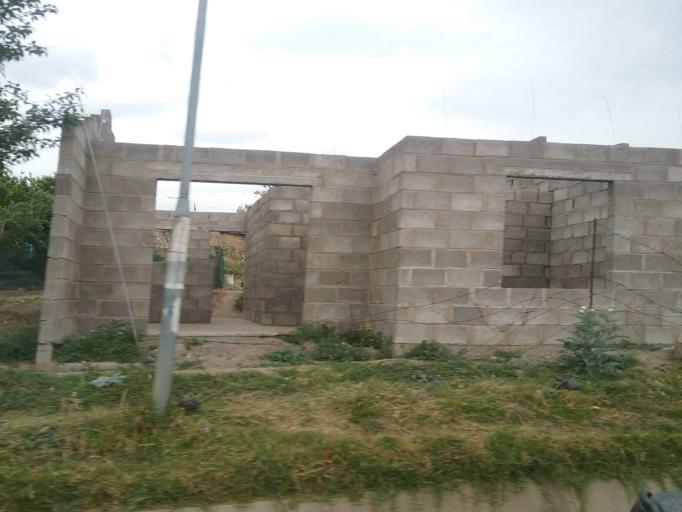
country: LS
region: Maseru
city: Maseru
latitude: -29.3256
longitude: 27.5080
